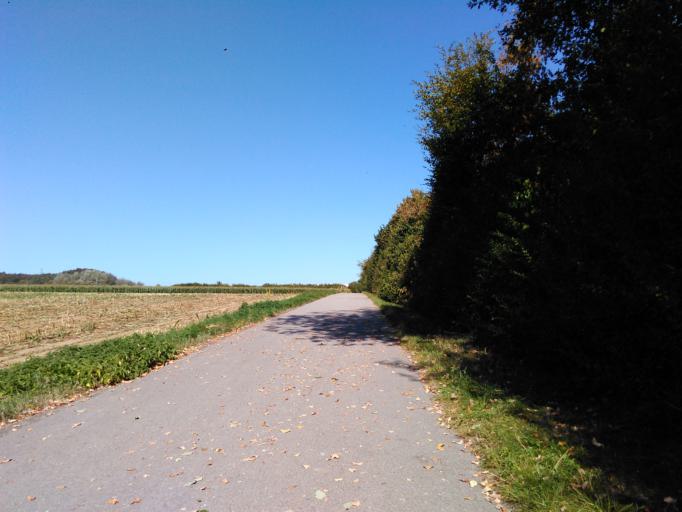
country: LU
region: Diekirch
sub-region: Canton de Redange
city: Beckerich
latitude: 49.7216
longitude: 5.9033
